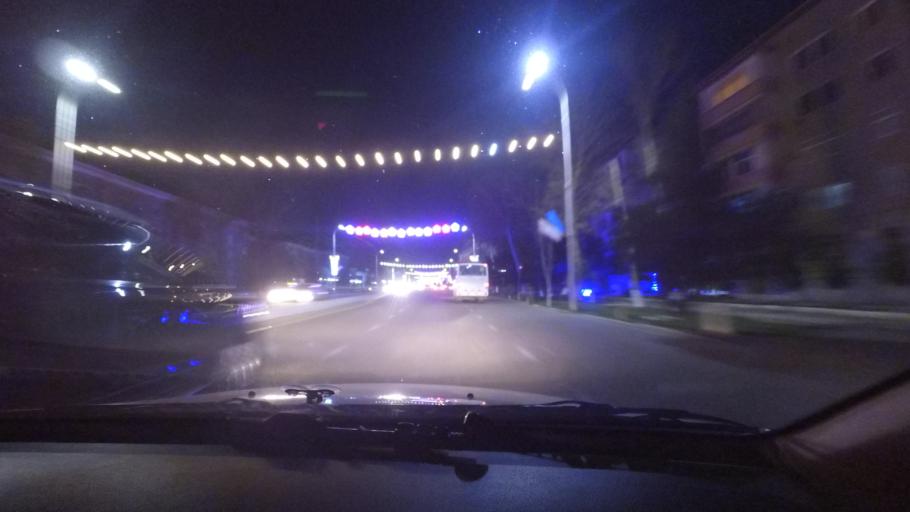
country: UZ
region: Bukhara
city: Bukhara
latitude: 39.7714
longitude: 64.4434
